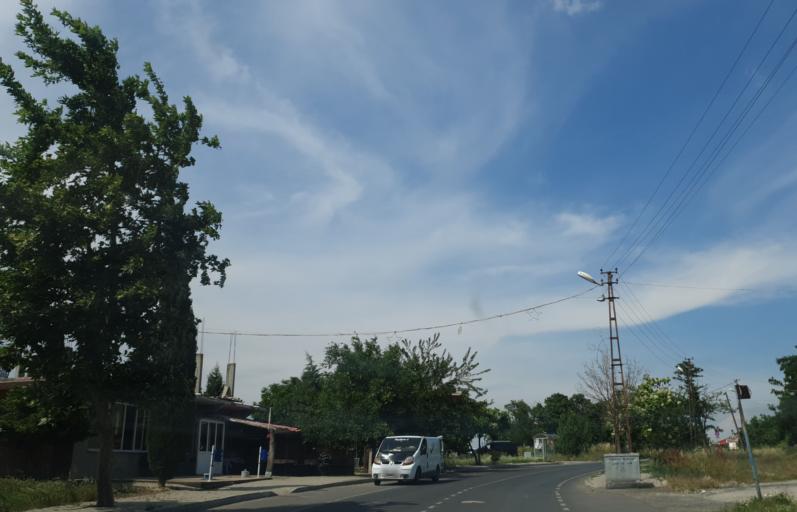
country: TR
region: Kirklareli
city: Buyukkaristiran
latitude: 41.2604
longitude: 27.6392
